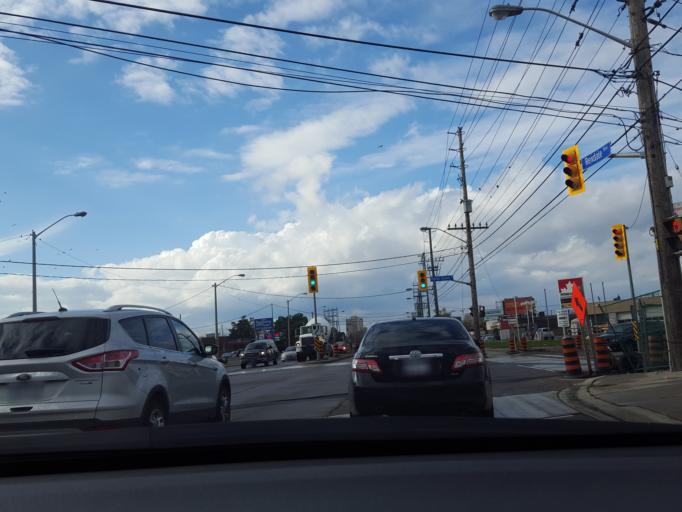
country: CA
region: Ontario
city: Etobicoke
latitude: 43.7138
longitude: -79.5807
